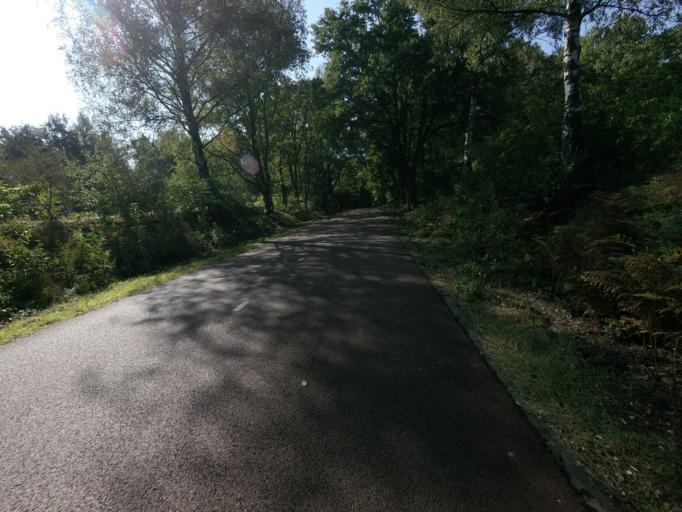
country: DE
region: North Rhine-Westphalia
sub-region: Regierungsbezirk Dusseldorf
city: Bruggen
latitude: 51.1793
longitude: 6.1445
